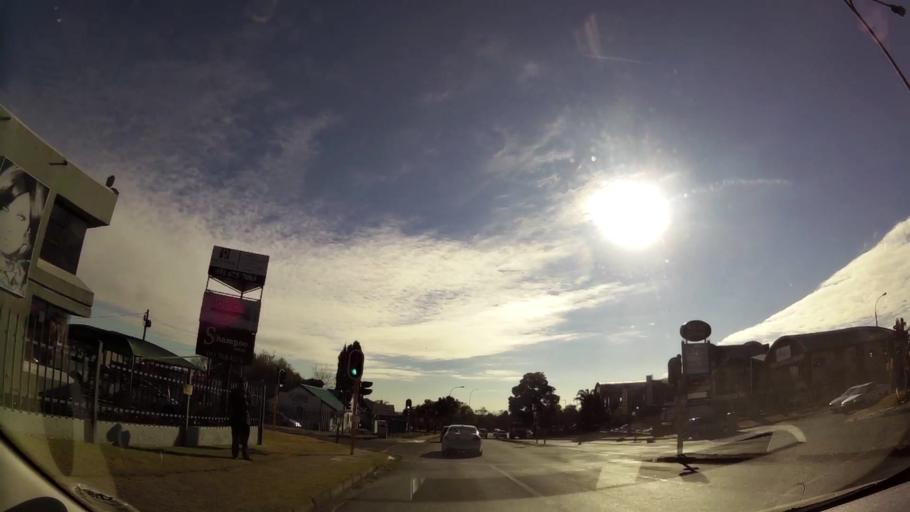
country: ZA
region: Gauteng
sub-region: City of Johannesburg Metropolitan Municipality
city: Roodepoort
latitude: -26.1249
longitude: 27.8464
